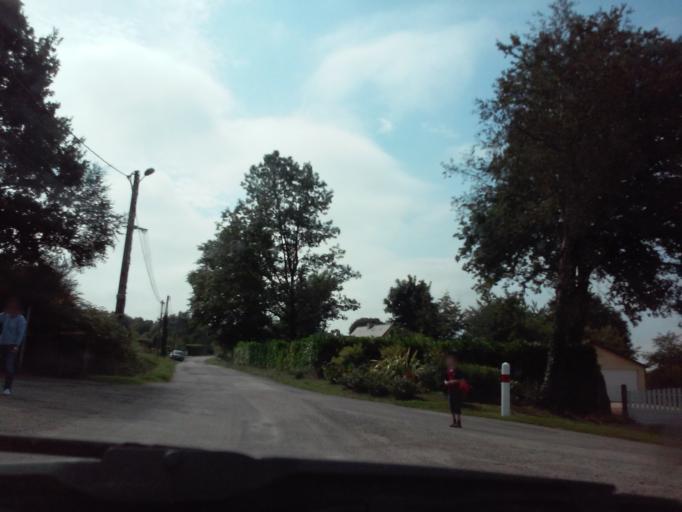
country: FR
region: Brittany
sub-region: Departement du Morbihan
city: Ploermel
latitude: 47.8872
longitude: -2.4114
